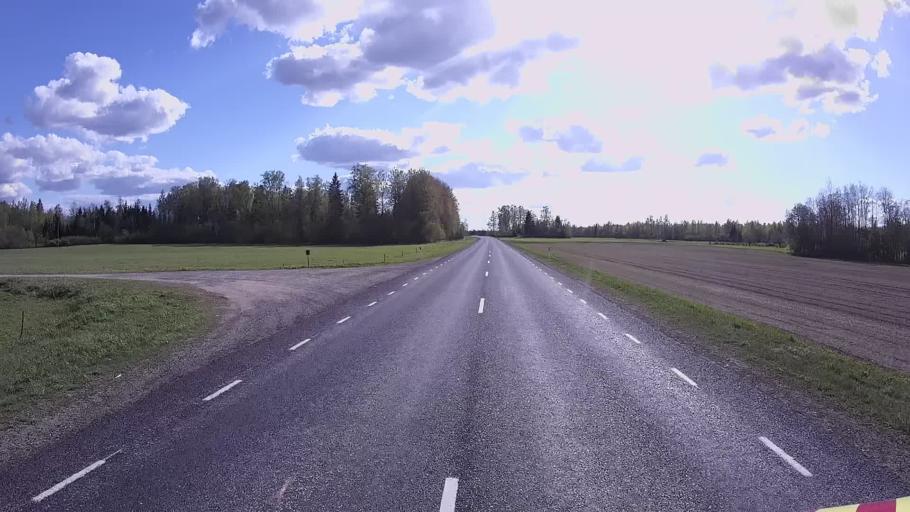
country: EE
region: Jogevamaa
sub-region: Poltsamaa linn
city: Poltsamaa
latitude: 58.7099
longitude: 26.1700
